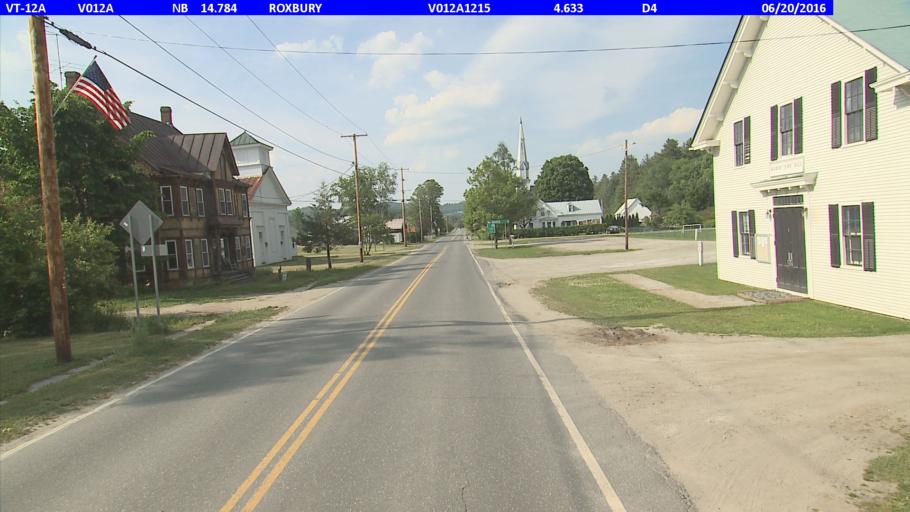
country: US
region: Vermont
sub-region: Washington County
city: Northfield
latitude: 44.0922
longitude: -72.7335
